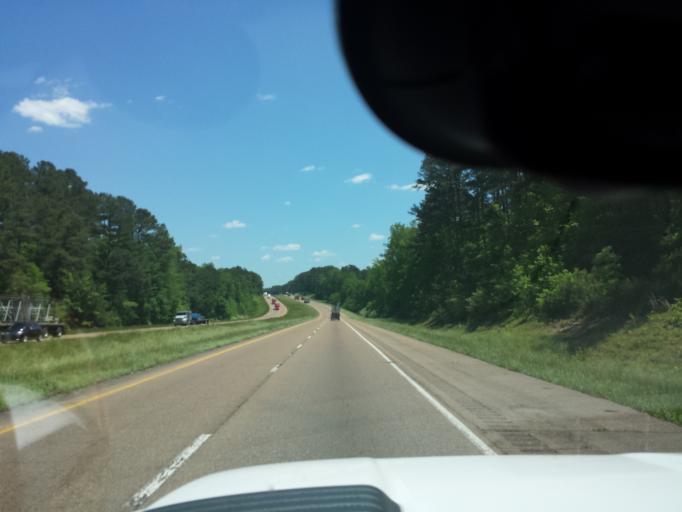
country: US
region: Mississippi
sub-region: Lauderdale County
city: Marion
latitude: 32.3889
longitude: -88.6043
